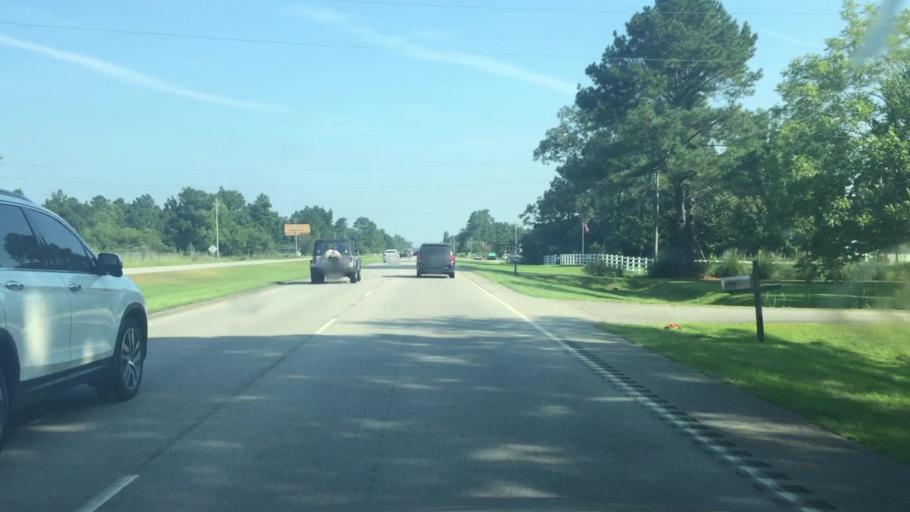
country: US
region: South Carolina
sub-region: Horry County
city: Little River
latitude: 33.9579
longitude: -78.7365
